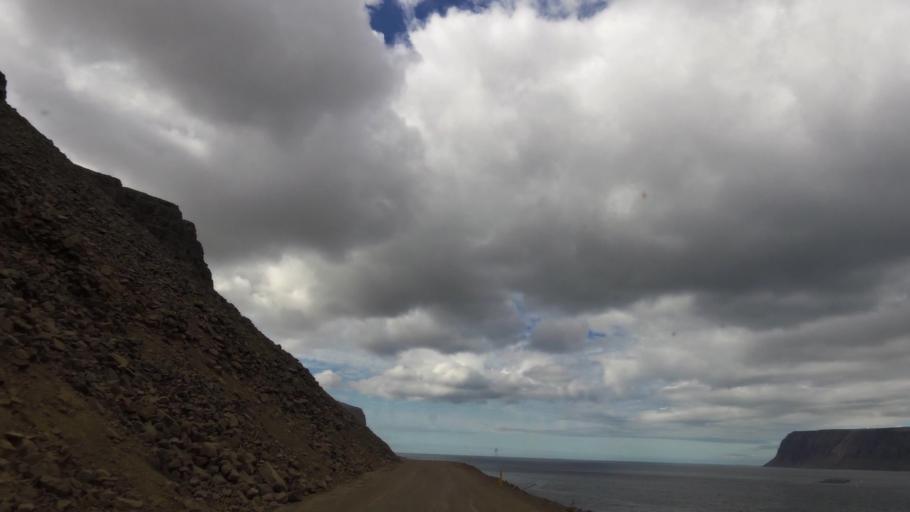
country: IS
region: West
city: Olafsvik
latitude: 65.5642
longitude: -24.0385
